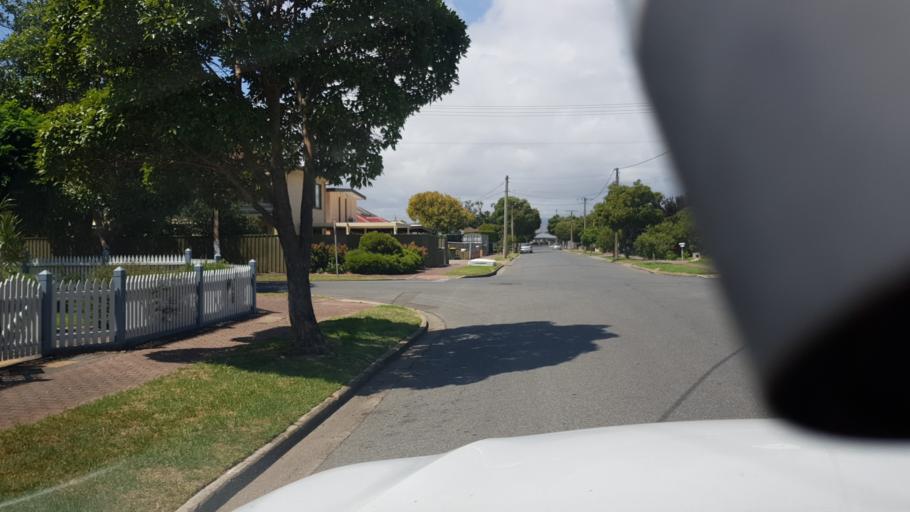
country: AU
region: South Australia
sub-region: Adelaide
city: Glenelg
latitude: -34.9905
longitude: 138.5233
